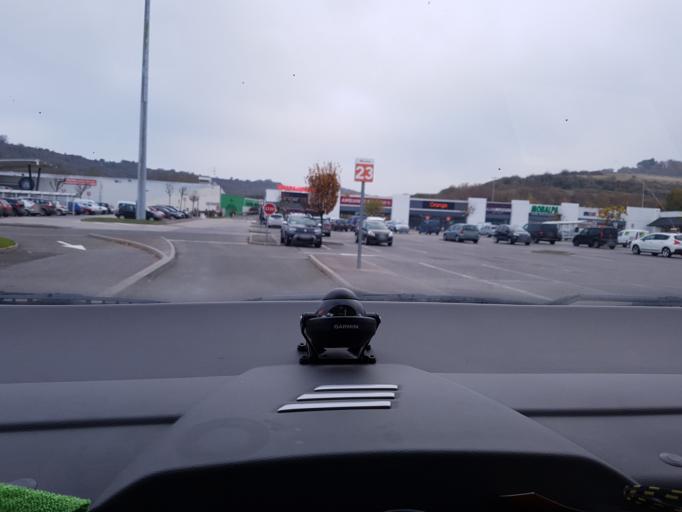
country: FR
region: Haute-Normandie
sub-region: Departement de la Seine-Maritime
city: Eu
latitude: 50.0609
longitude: 1.4085
